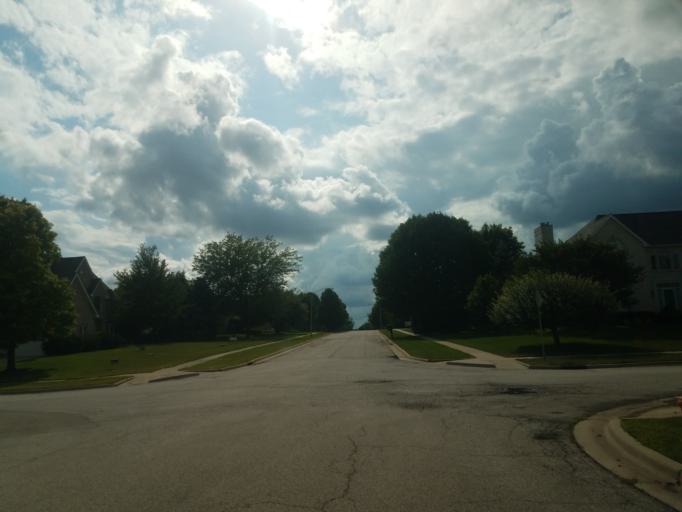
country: US
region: Illinois
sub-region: McLean County
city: Normal
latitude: 40.5078
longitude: -88.9129
